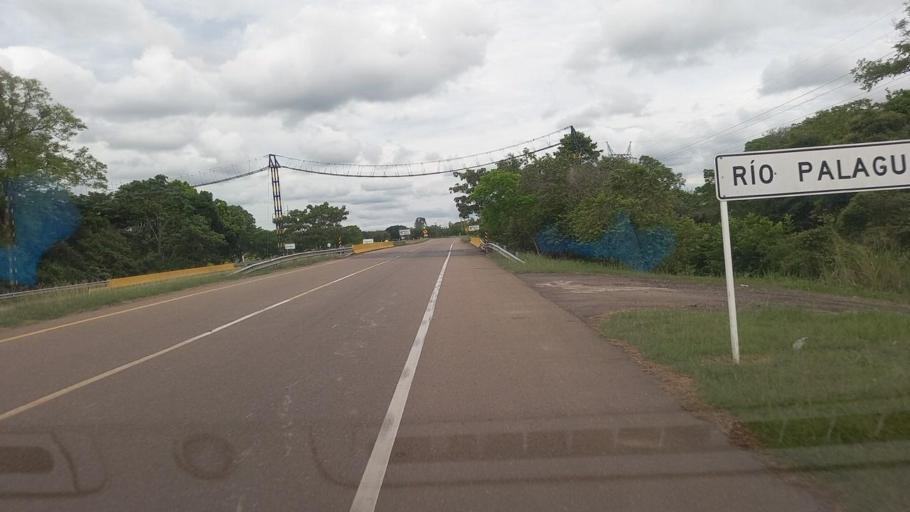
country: CO
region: Boyaca
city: Puerto Boyaca
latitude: 6.0703
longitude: -74.5544
